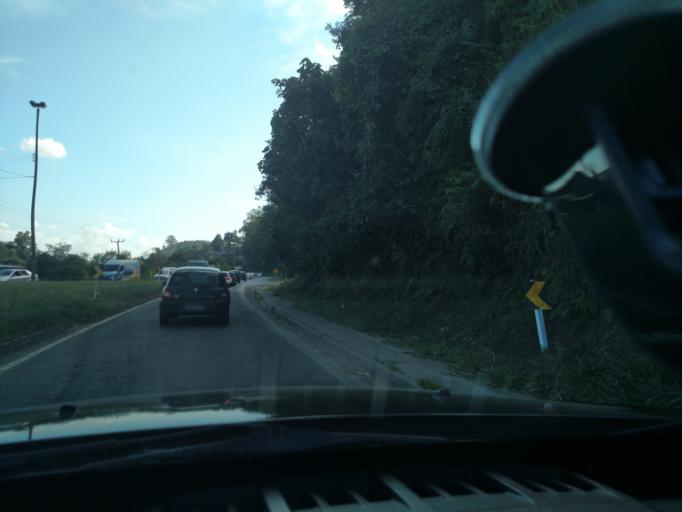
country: BR
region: Santa Catarina
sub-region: Rio Do Sul
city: Rio do Sul
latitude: -27.2212
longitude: -49.6609
